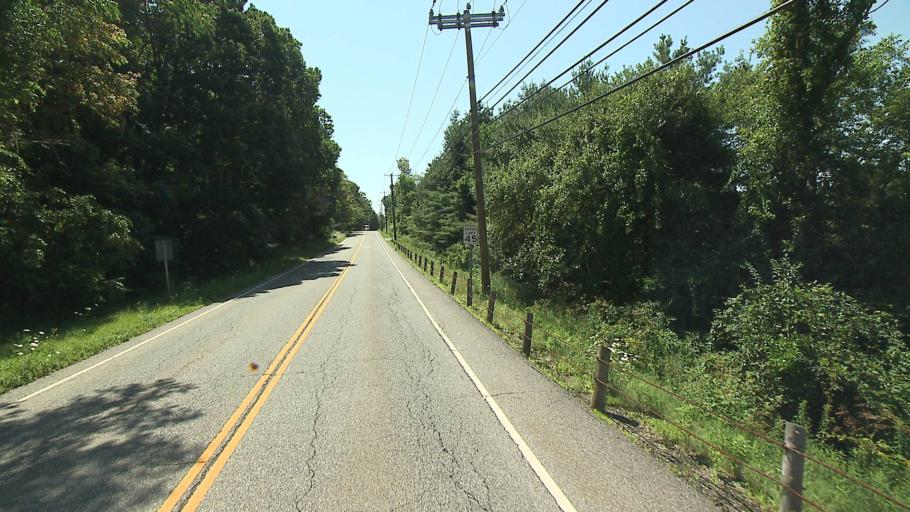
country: US
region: Connecticut
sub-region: Litchfield County
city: Kent
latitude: 41.8392
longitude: -73.4319
